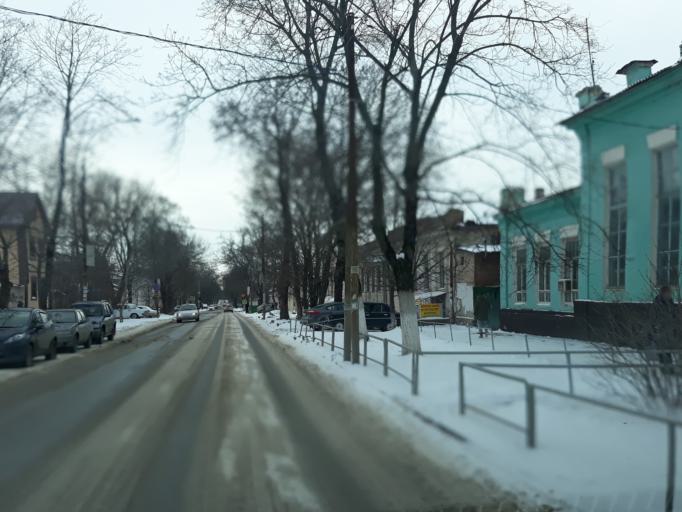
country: RU
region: Rostov
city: Taganrog
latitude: 47.2116
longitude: 38.9248
